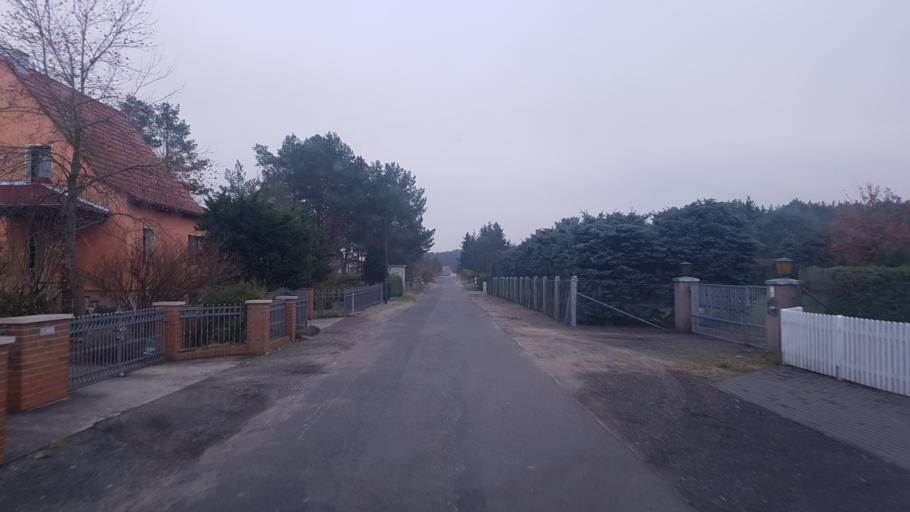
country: DE
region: Brandenburg
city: Gross Kreutz
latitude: 52.3534
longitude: 12.7532
